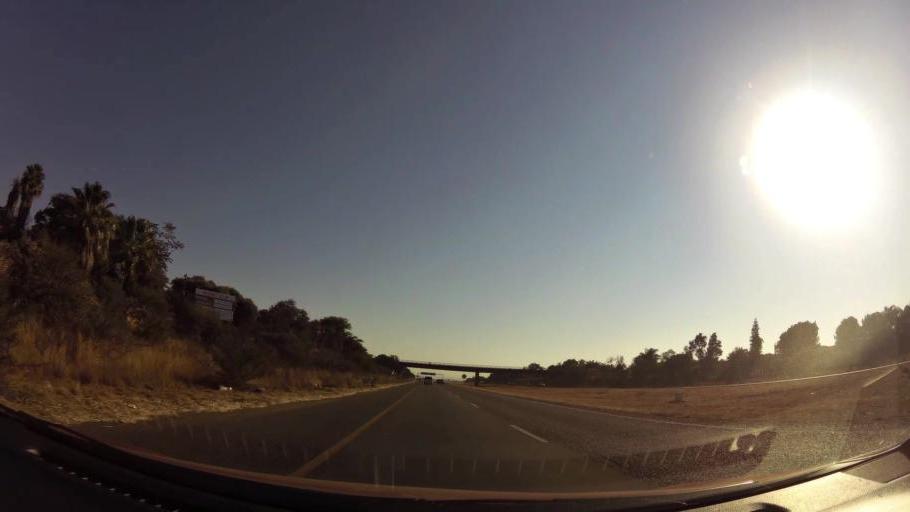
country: ZA
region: Gauteng
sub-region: City of Tshwane Metropolitan Municipality
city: Pretoria
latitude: -25.6678
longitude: 28.1155
